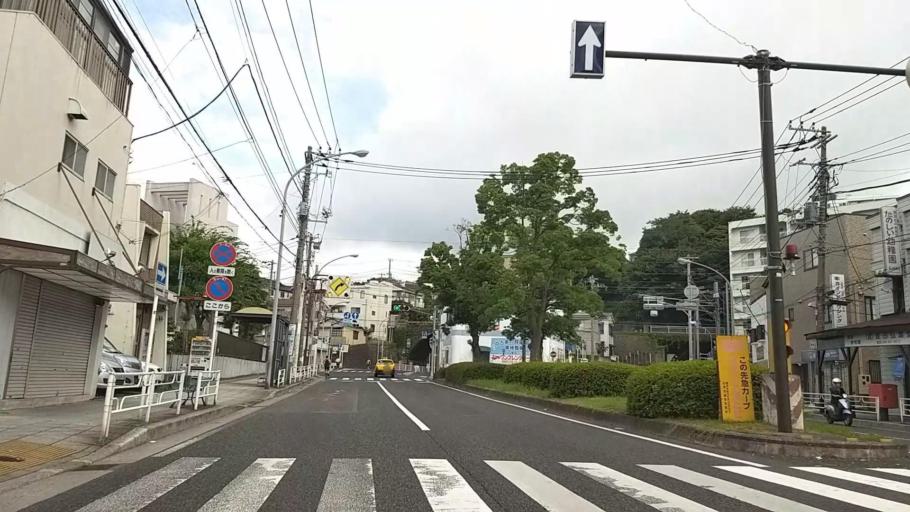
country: JP
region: Kanagawa
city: Yokohama
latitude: 35.4339
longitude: 139.6469
